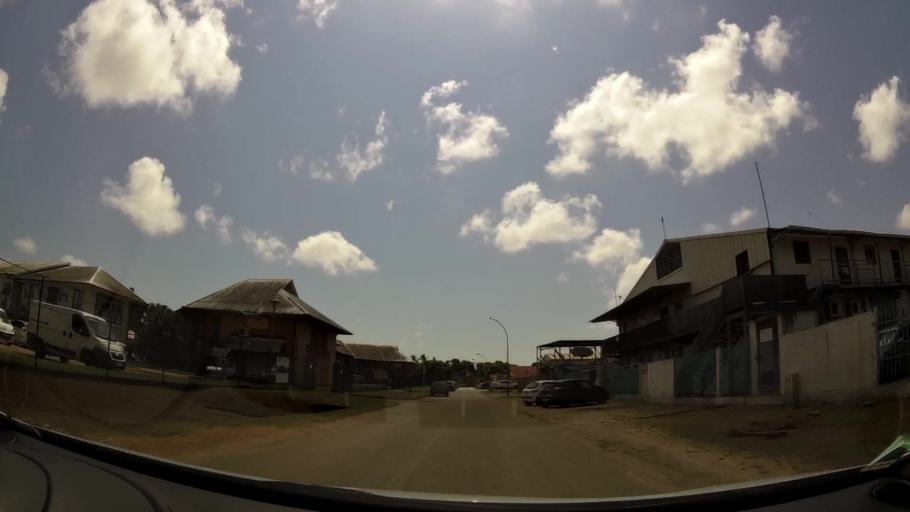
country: GF
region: Guyane
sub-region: Guyane
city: Cayenne
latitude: 4.9288
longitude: -52.3283
